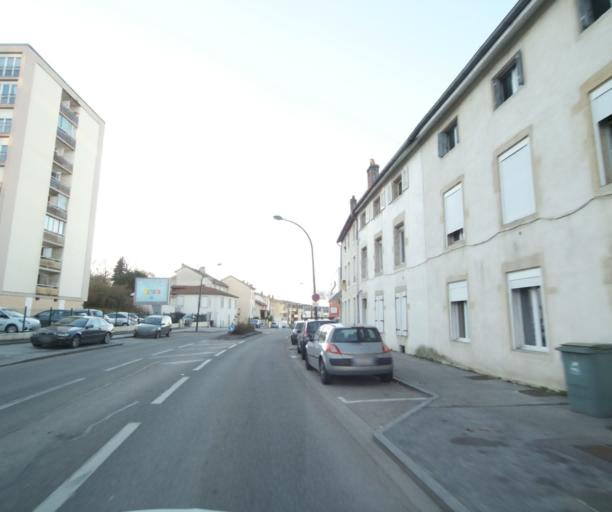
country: FR
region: Lorraine
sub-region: Departement de Meurthe-et-Moselle
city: Jarville-la-Malgrange
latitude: 48.6673
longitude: 6.2103
